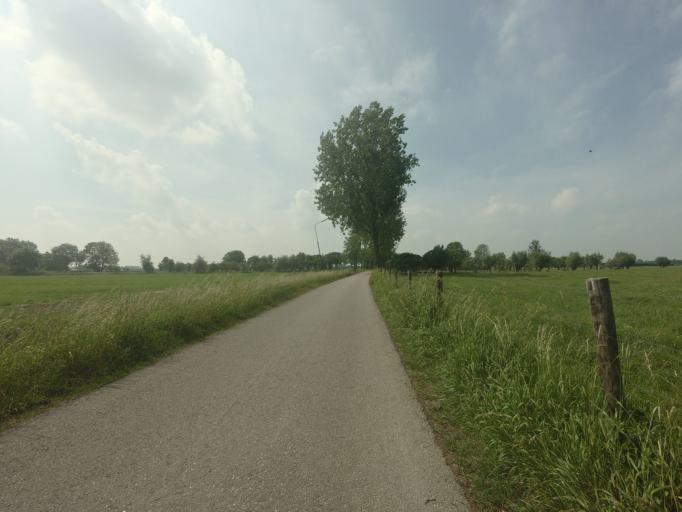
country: NL
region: Utrecht
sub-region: Gemeente IJsselstein
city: IJsselstein
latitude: 52.0065
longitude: 5.0608
